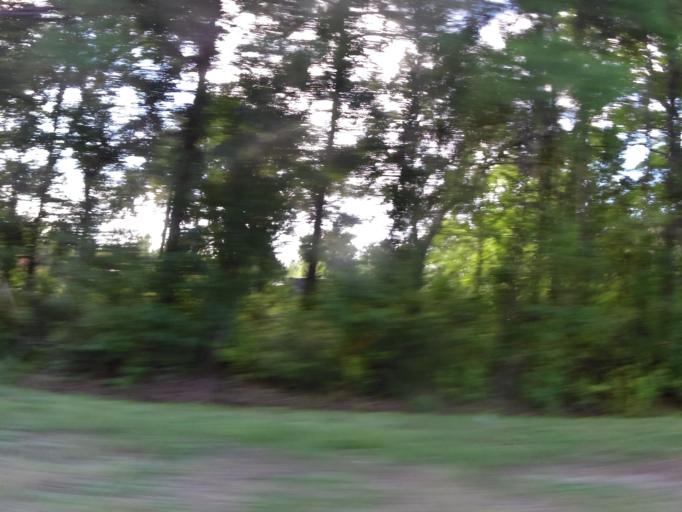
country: US
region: Georgia
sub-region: Glynn County
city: Country Club Estates
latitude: 31.2336
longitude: -81.4533
